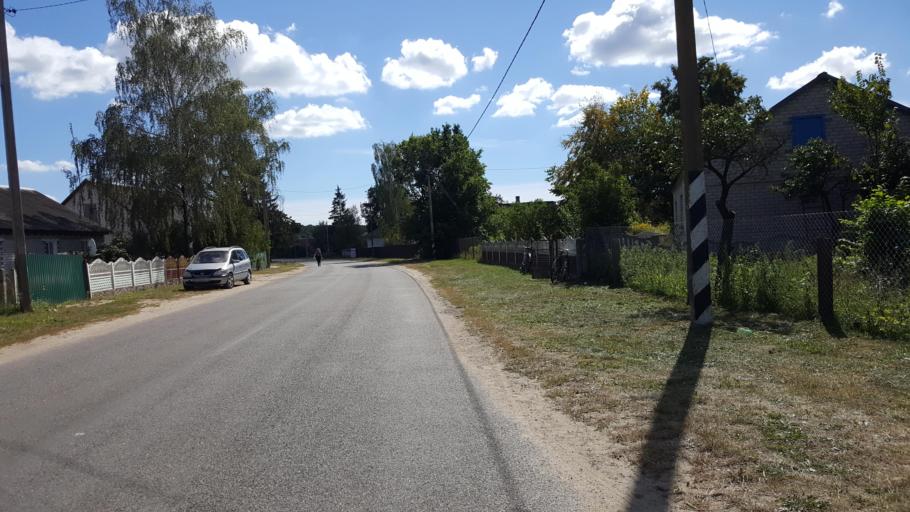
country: BY
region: Brest
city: Vysokaye
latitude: 52.2785
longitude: 23.3140
